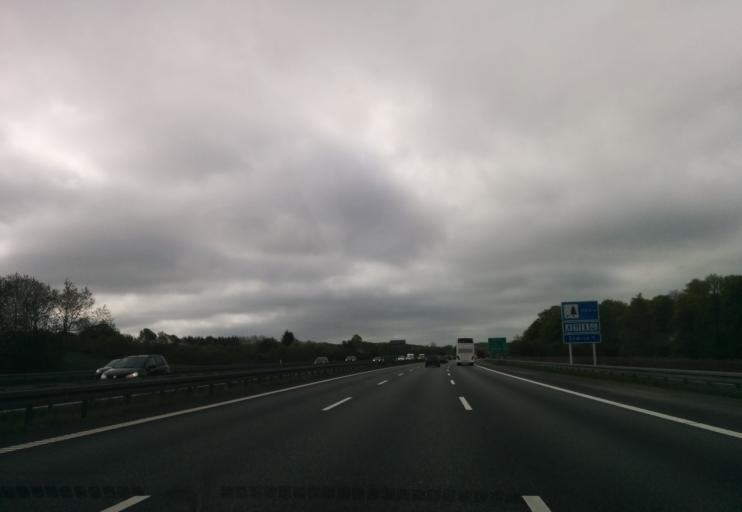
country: DK
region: South Denmark
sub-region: Vejle Kommune
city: Vejle
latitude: 55.6570
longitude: 9.5597
